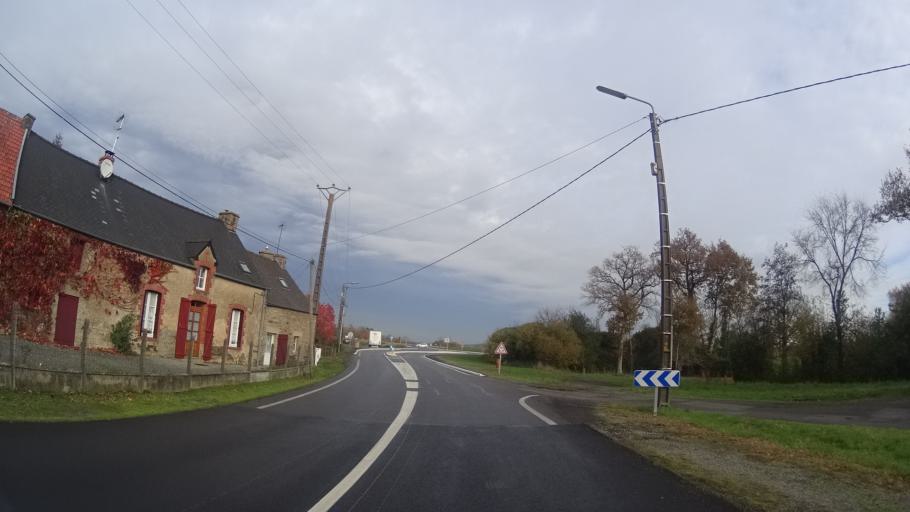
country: FR
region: Brittany
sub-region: Departement du Morbihan
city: Saint-Jean-la-Poterie
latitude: 47.6260
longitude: -2.1026
